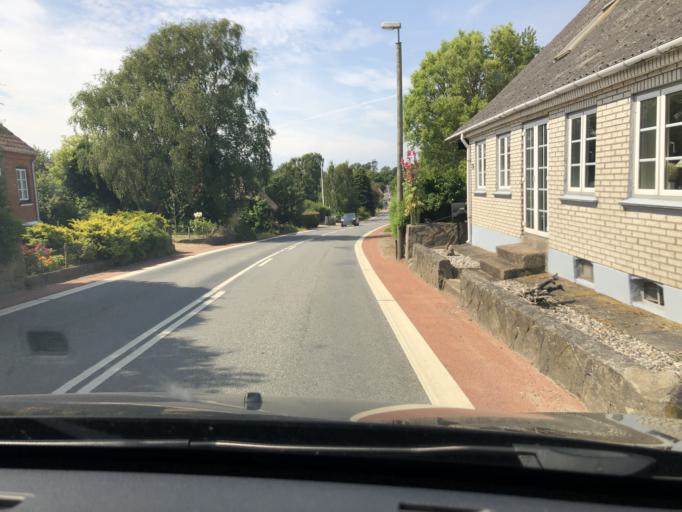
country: DK
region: South Denmark
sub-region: AEro Kommune
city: AEroskobing
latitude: 54.8895
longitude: 10.3149
